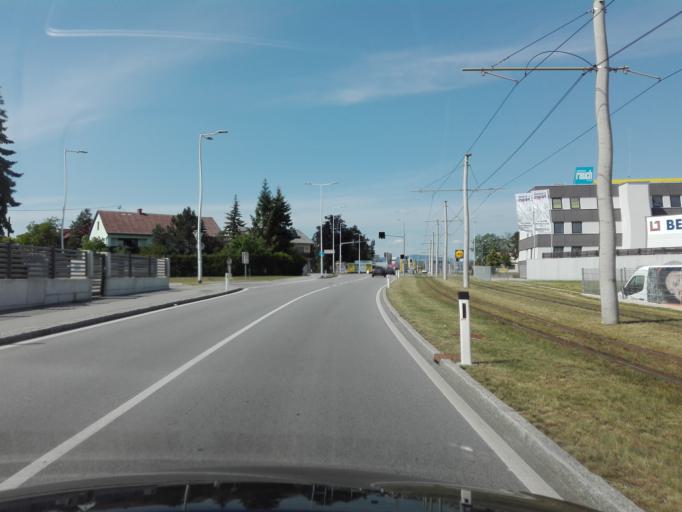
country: AT
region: Upper Austria
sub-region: Politischer Bezirk Linz-Land
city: Traun
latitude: 48.2288
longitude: 14.2336
